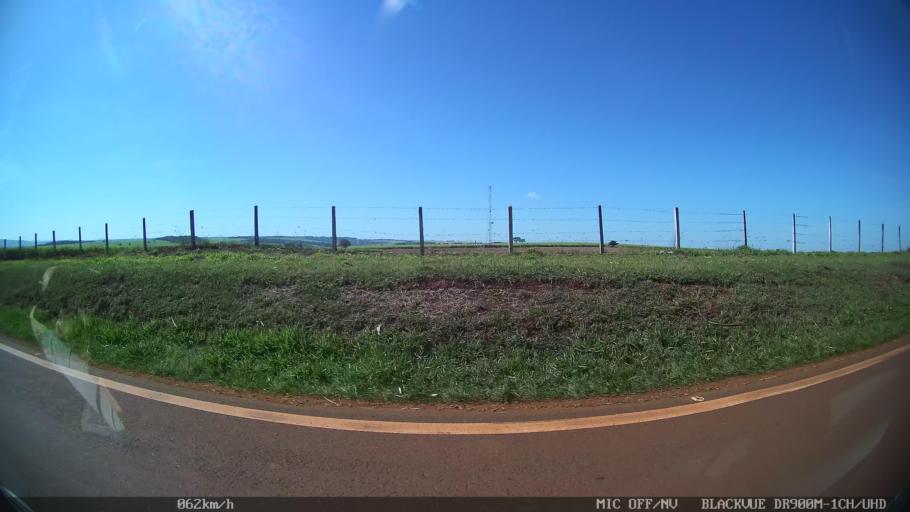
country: BR
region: Sao Paulo
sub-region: Franca
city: Franca
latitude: -20.6748
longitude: -47.4951
